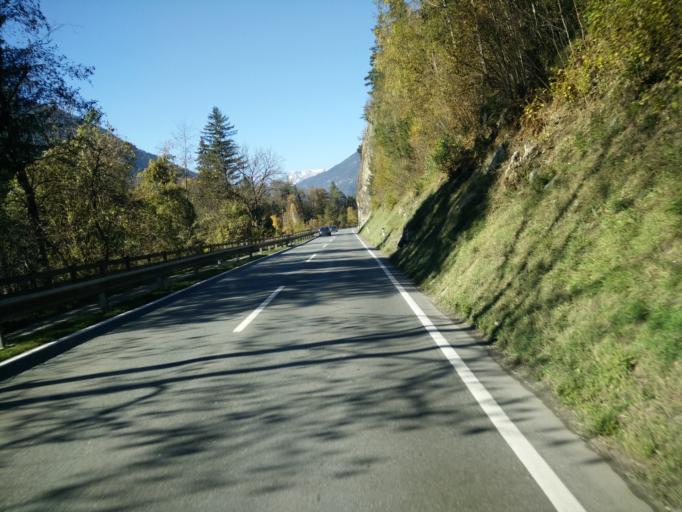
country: AT
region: Tyrol
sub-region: Politischer Bezirk Imst
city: Sautens
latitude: 47.2076
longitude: 10.8762
